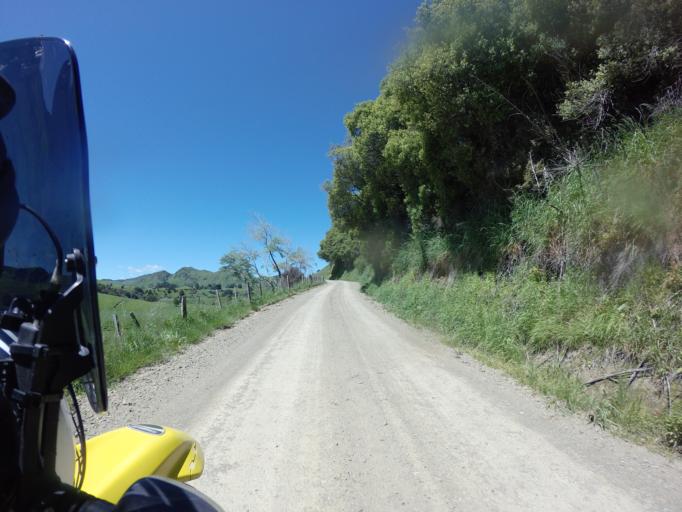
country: NZ
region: Bay of Plenty
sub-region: Opotiki District
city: Opotiki
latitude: -38.3943
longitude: 177.4592
